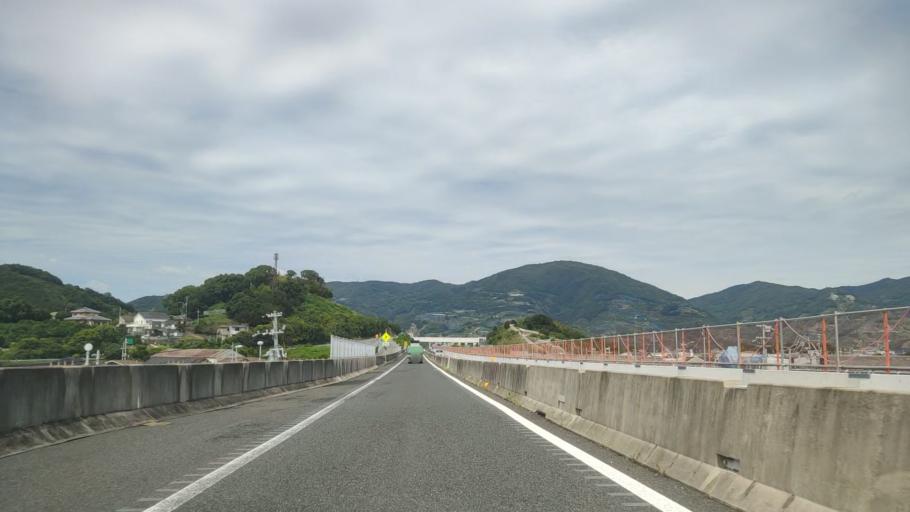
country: JP
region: Wakayama
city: Kainan
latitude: 34.0560
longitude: 135.2008
